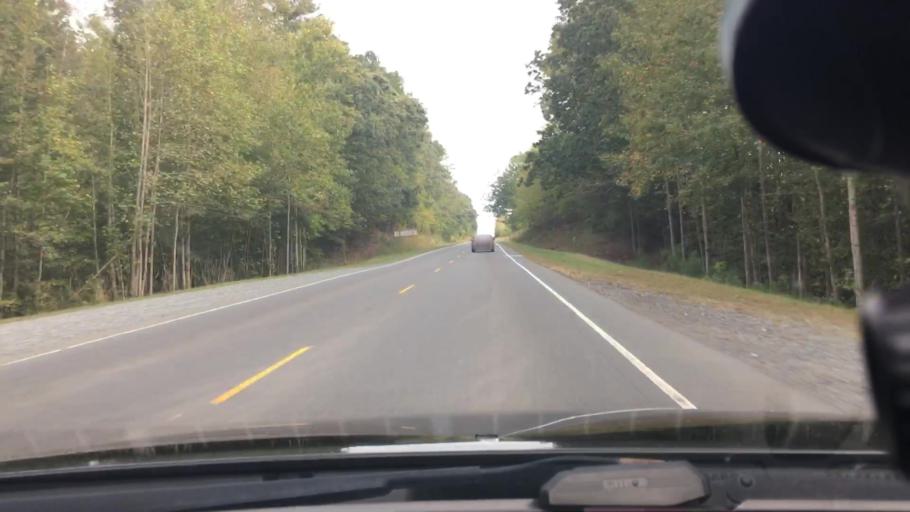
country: US
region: North Carolina
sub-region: Montgomery County
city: Mount Gilead
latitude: 35.3101
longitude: -80.0436
